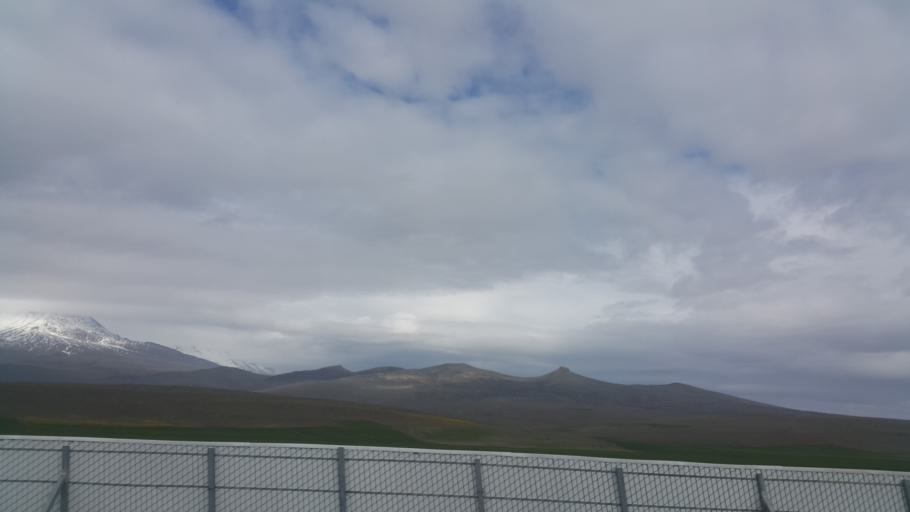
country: TR
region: Aksaray
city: Taspinar
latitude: 38.0715
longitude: 34.0326
